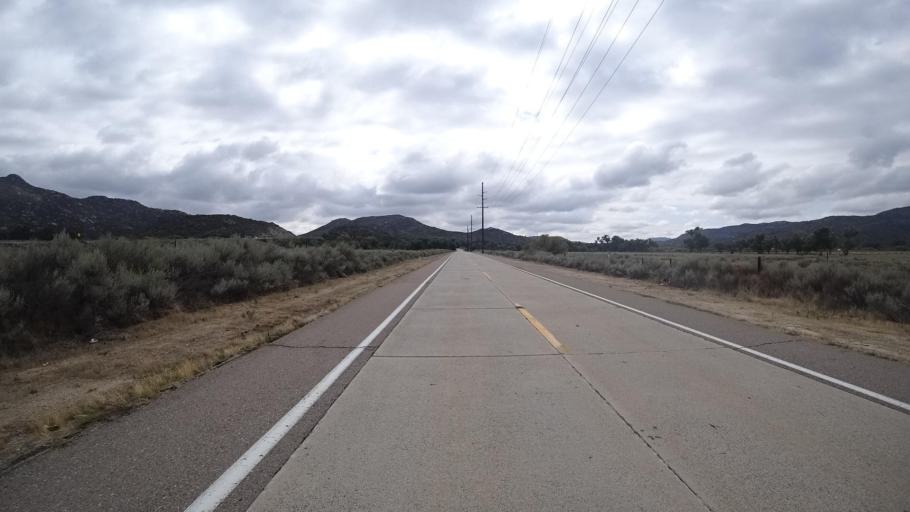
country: US
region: California
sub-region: San Diego County
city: Pine Valley
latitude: 32.7384
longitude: -116.4820
